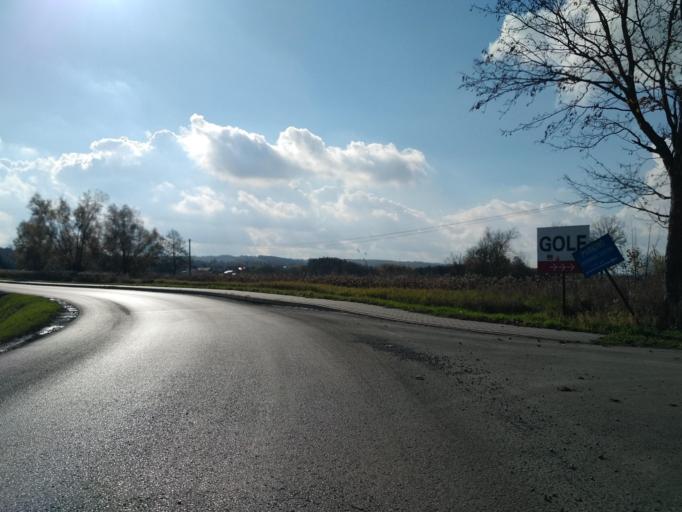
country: PL
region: Subcarpathian Voivodeship
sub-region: Powiat rzeszowski
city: Trzciana
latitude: 50.0851
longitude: 21.8402
